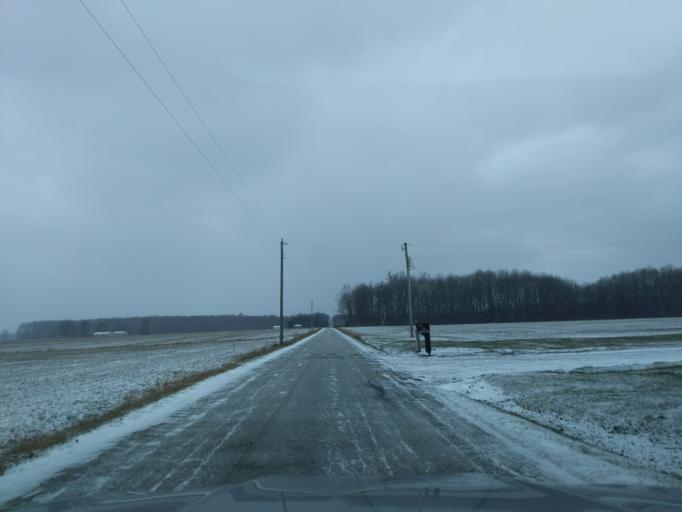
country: US
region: Indiana
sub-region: Decatur County
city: Greensburg
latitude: 39.2340
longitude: -85.4745
